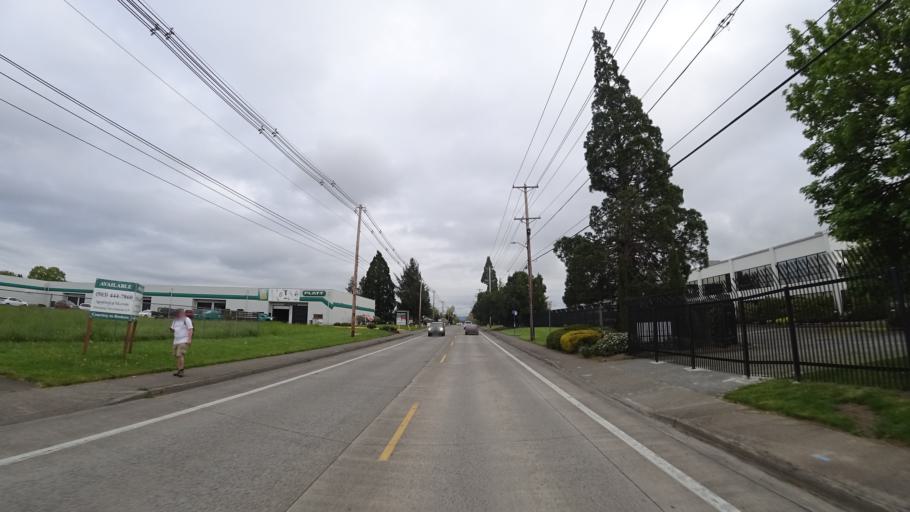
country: US
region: Oregon
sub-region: Washington County
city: Hillsboro
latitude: 45.5335
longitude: -122.9570
